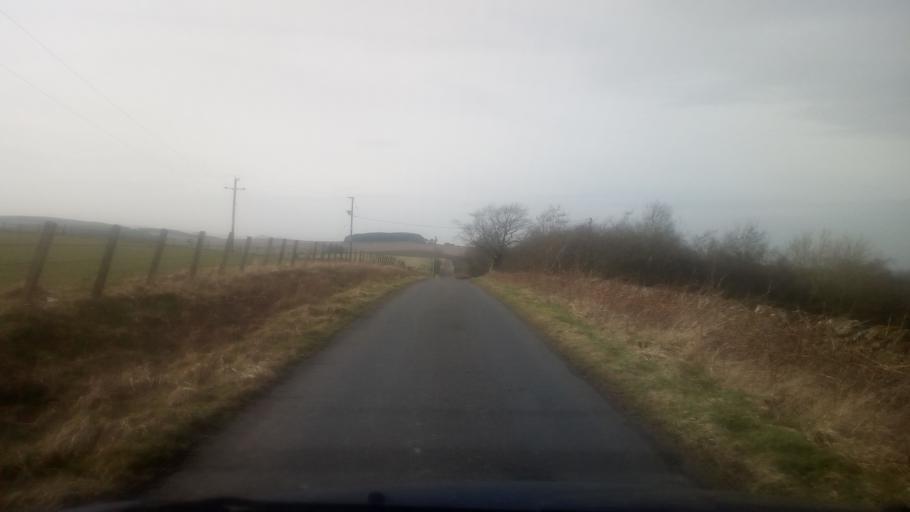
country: GB
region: Scotland
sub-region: The Scottish Borders
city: Hawick
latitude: 55.4040
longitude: -2.6711
